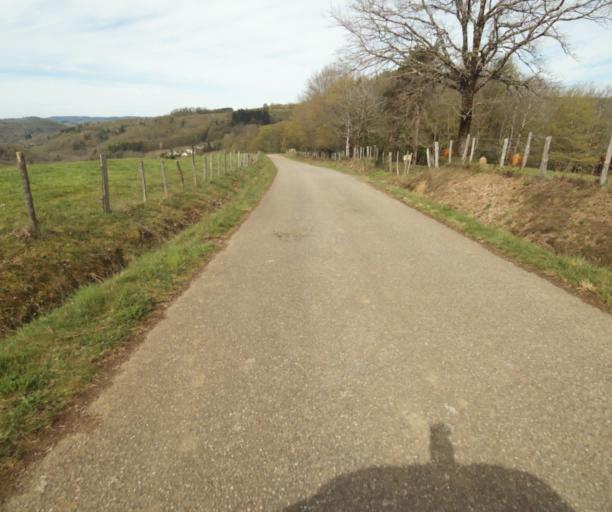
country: FR
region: Limousin
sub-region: Departement de la Correze
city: Laguenne
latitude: 45.2504
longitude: 1.8306
